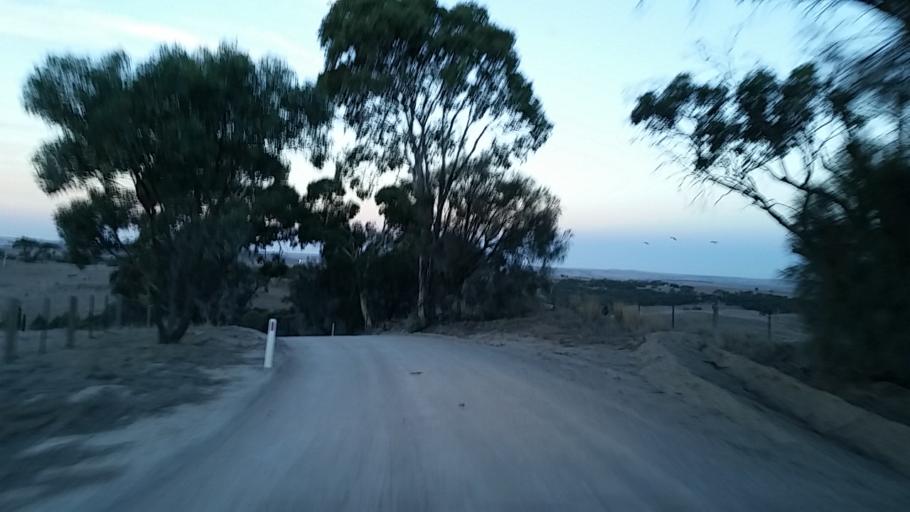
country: AU
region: South Australia
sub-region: Mount Barker
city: Nairne
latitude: -35.0908
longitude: 138.9482
